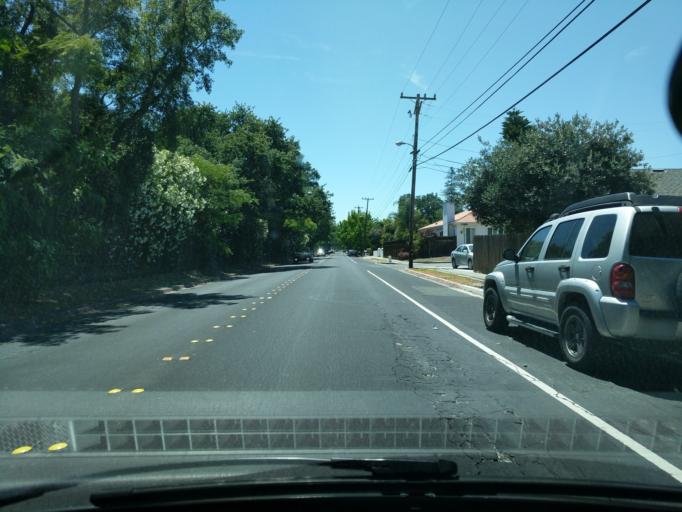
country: US
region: California
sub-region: Contra Costa County
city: Waldon
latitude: 37.9359
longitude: -122.0435
